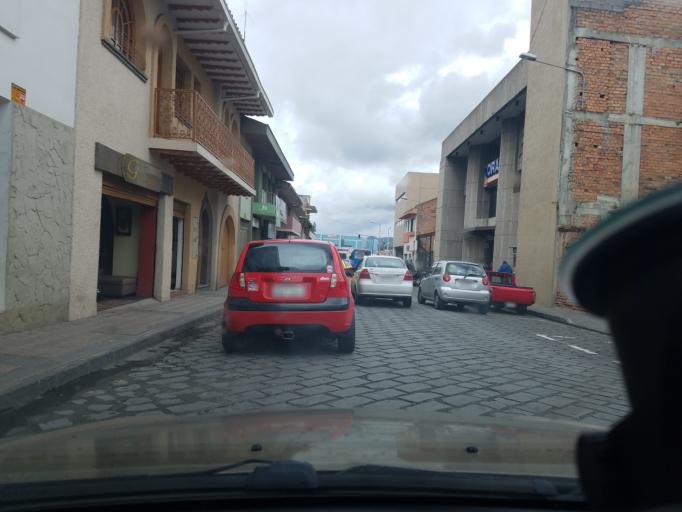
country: EC
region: Azuay
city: Cuenca
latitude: -2.8995
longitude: -78.9976
